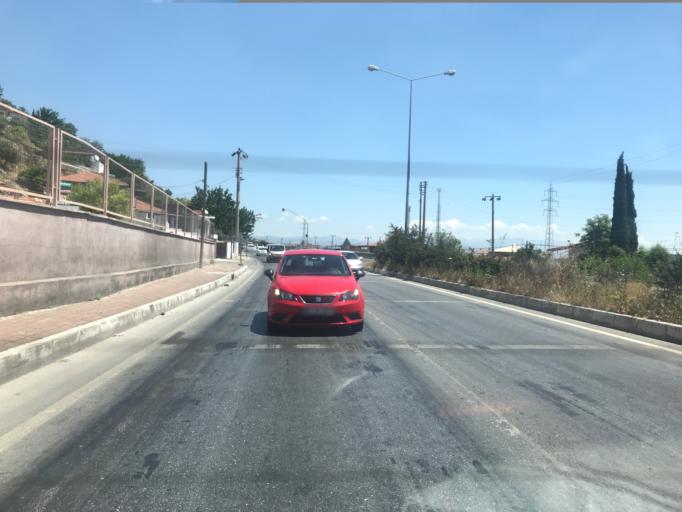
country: TR
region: Aydin
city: Soeke
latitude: 37.7845
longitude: 27.4638
